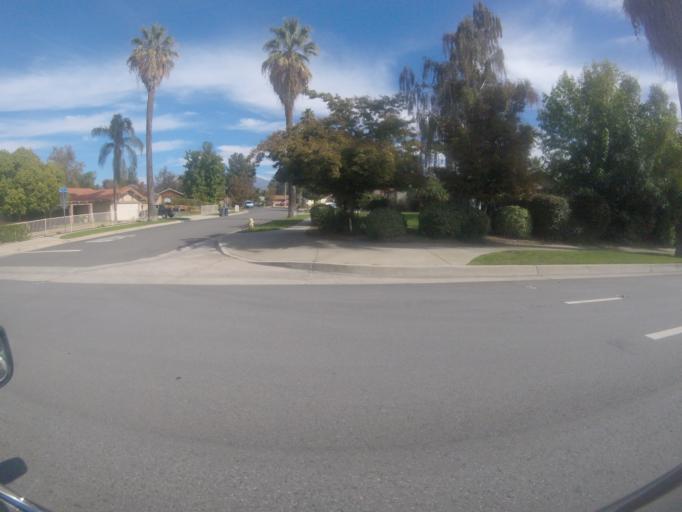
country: US
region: California
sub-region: San Bernardino County
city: Redlands
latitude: 34.0539
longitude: -117.1563
